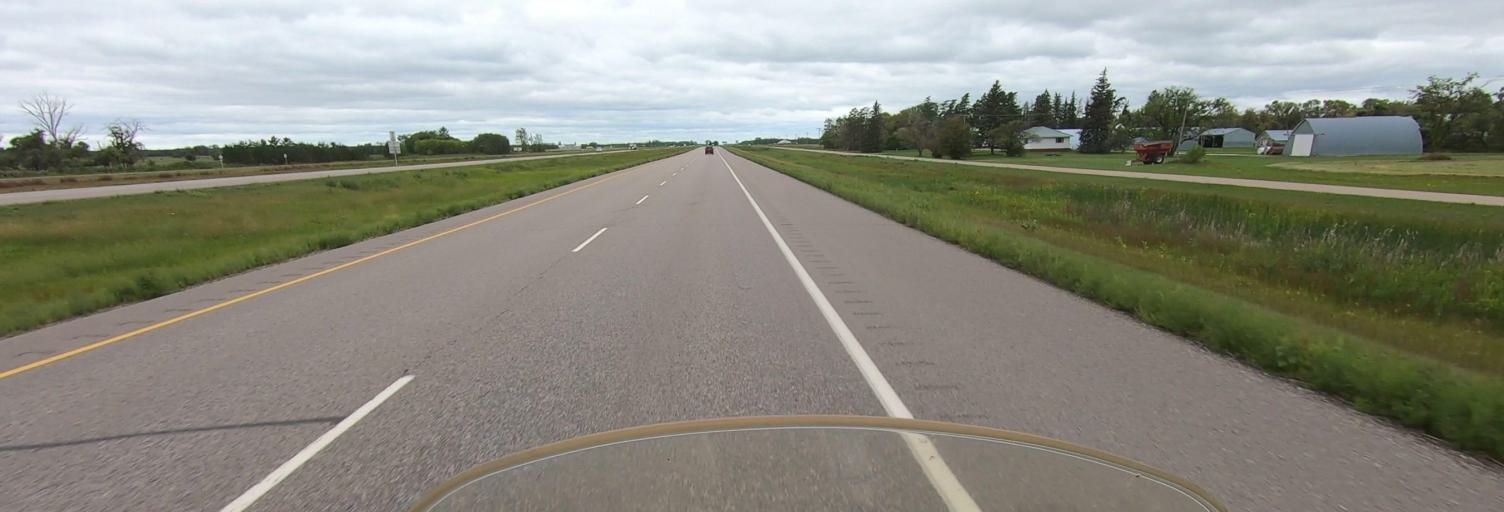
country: CA
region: Manitoba
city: Portage la Prairie
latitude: 49.9752
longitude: -98.6314
